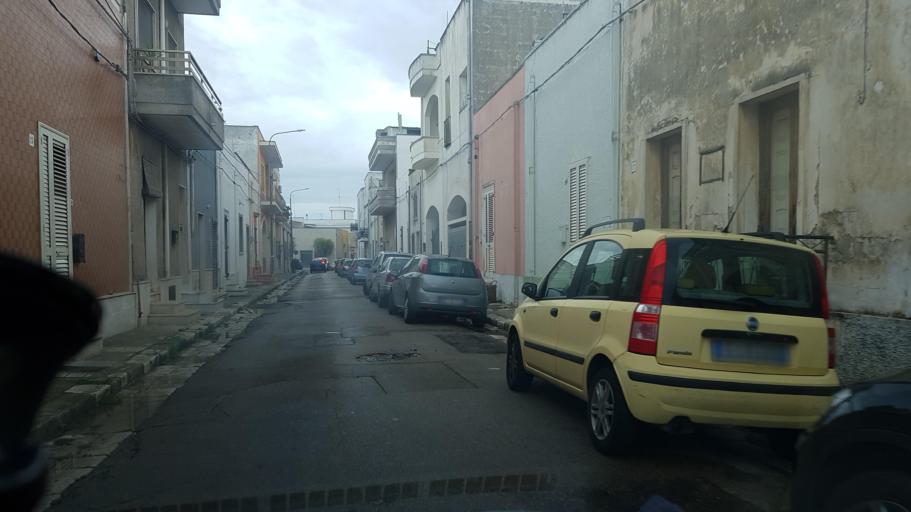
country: IT
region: Apulia
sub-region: Provincia di Lecce
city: Salice Salentino
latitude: 40.3843
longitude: 17.9621
